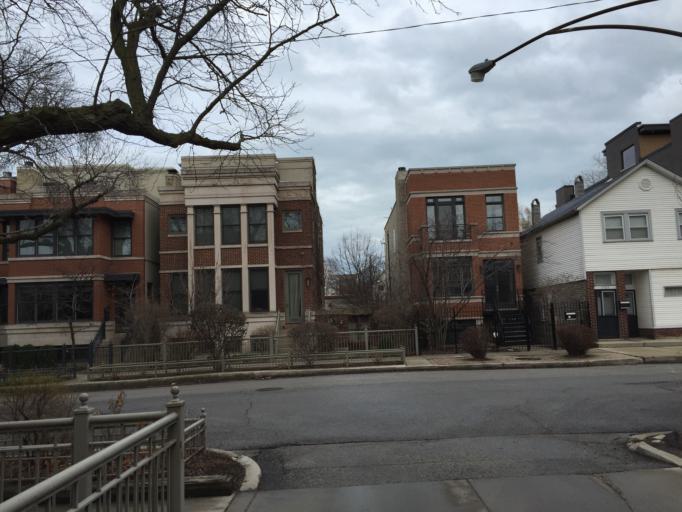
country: US
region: Illinois
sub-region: Cook County
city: Chicago
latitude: 41.9139
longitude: -87.6729
